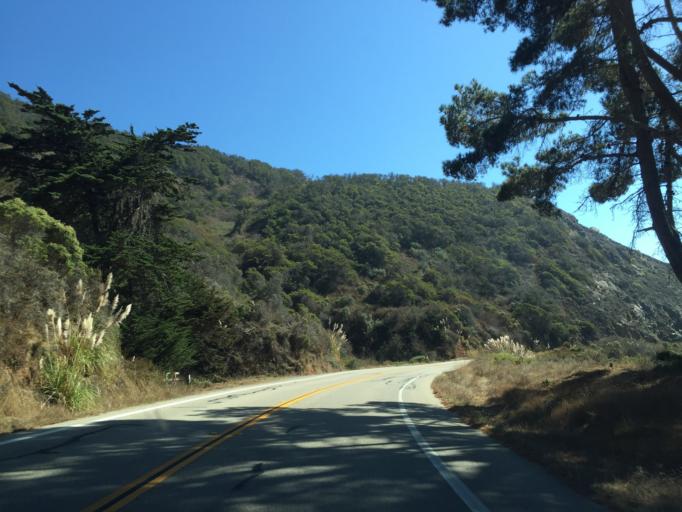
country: US
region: California
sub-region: Monterey County
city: Greenfield
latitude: 36.0765
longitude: -121.6067
